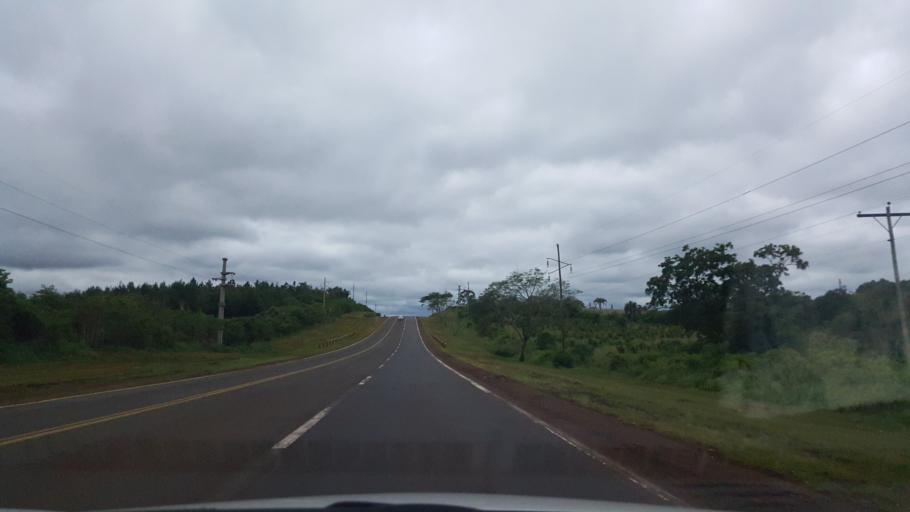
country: AR
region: Misiones
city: Capiovi
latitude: -26.9461
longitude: -55.0866
